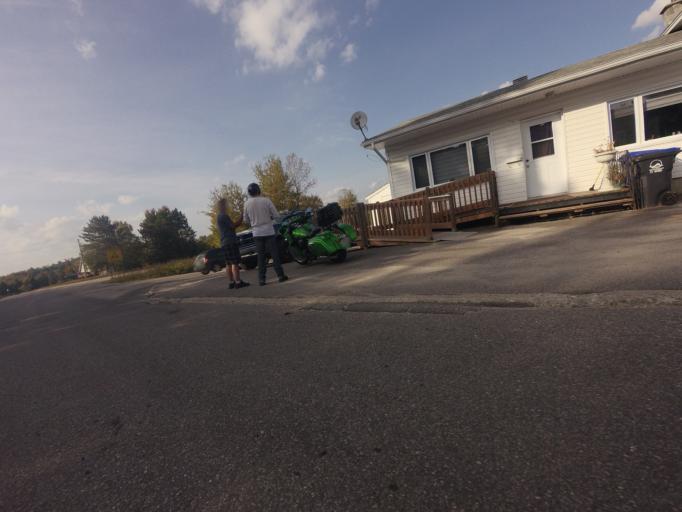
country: CA
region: Quebec
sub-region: Outaouais
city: Maniwaki
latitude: 46.3637
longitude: -75.9872
